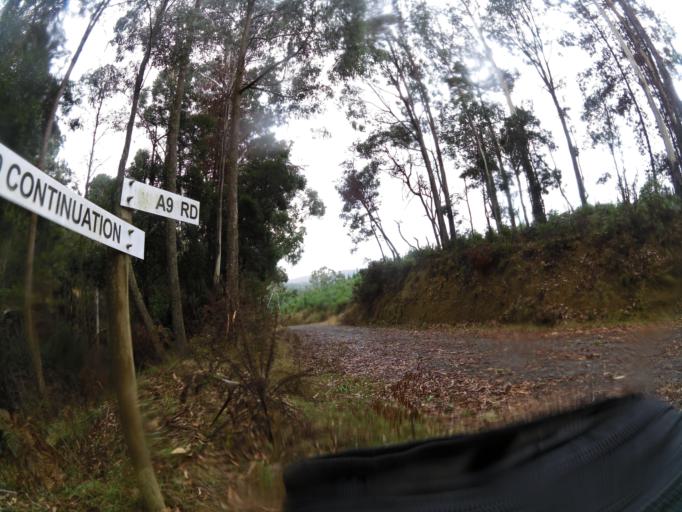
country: AU
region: New South Wales
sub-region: Greater Hume Shire
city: Holbrook
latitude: -36.2160
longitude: 147.5658
